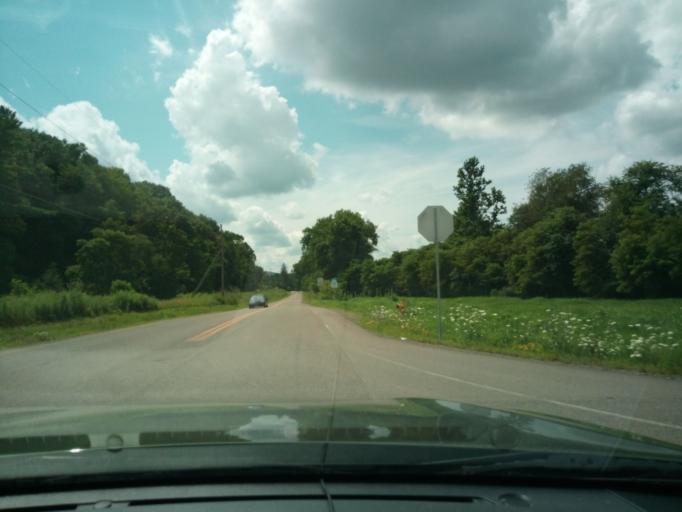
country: US
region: Pennsylvania
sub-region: Bradford County
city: South Waverly
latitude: 41.9975
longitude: -76.5879
